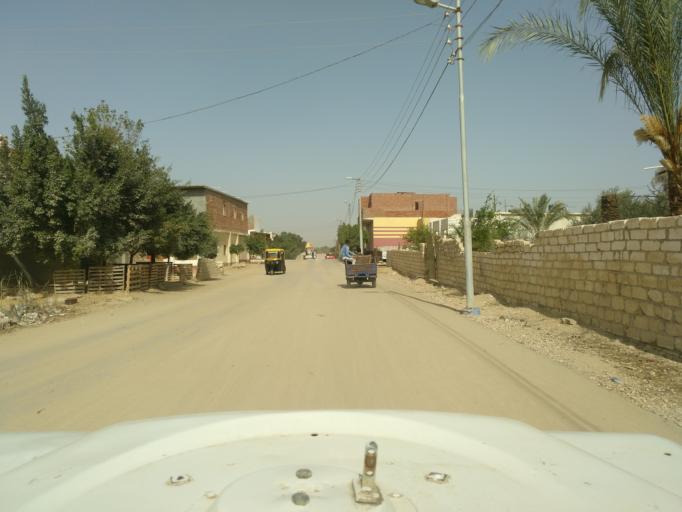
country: EG
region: Al Buhayrah
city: Beheira
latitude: 30.3839
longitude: 30.3415
